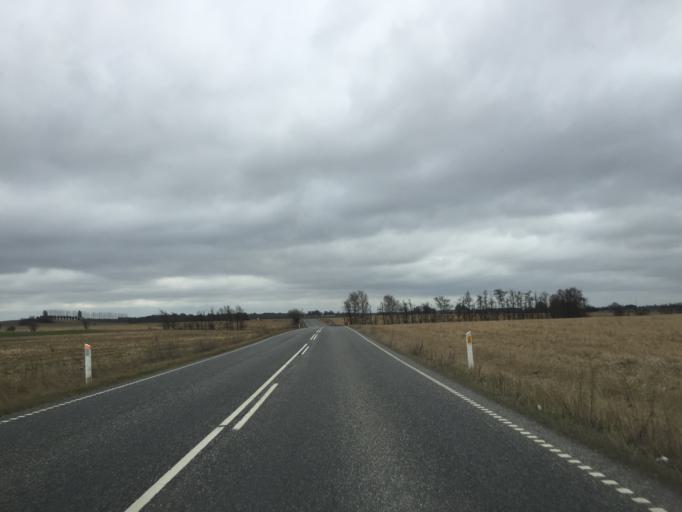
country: DK
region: Capital Region
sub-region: Allerod Kommune
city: Lynge
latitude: 55.8846
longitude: 12.2752
